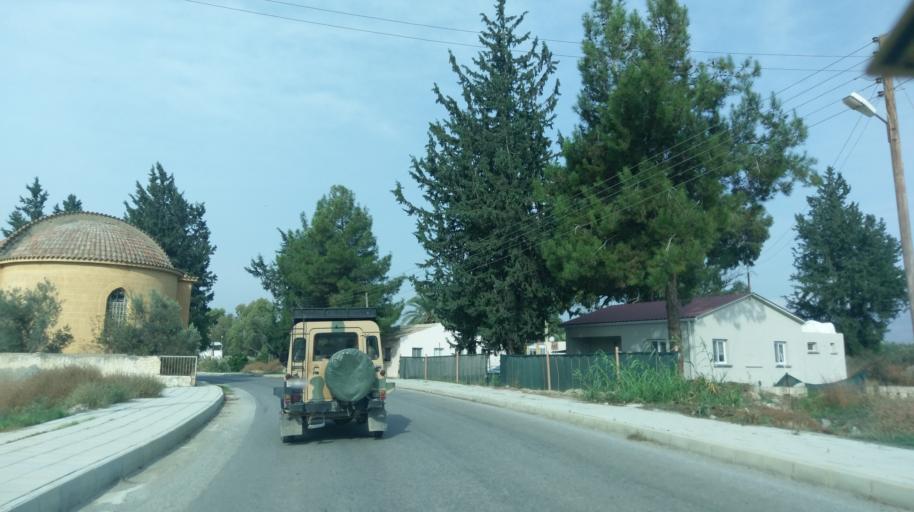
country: CY
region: Lefkosia
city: Mammari
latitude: 35.2302
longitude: 33.1689
